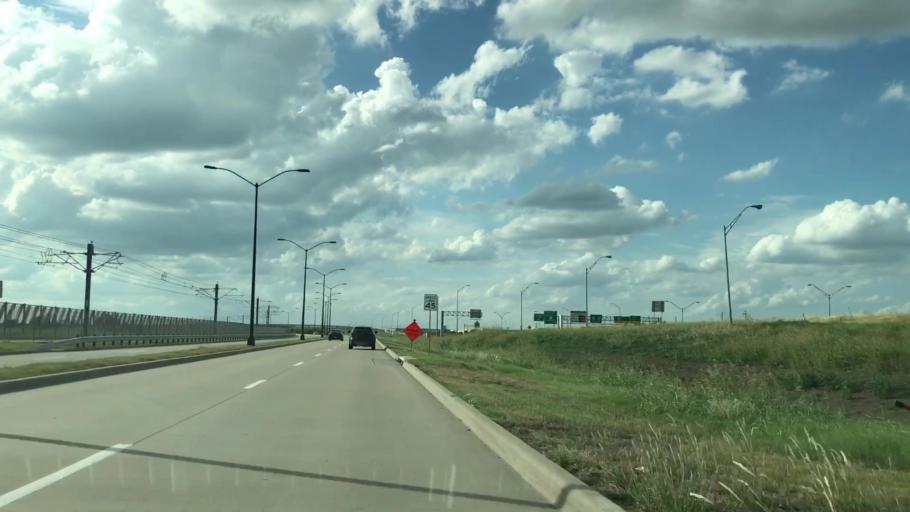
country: US
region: Texas
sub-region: Dallas County
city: Coppell
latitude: 32.9218
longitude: -97.0234
